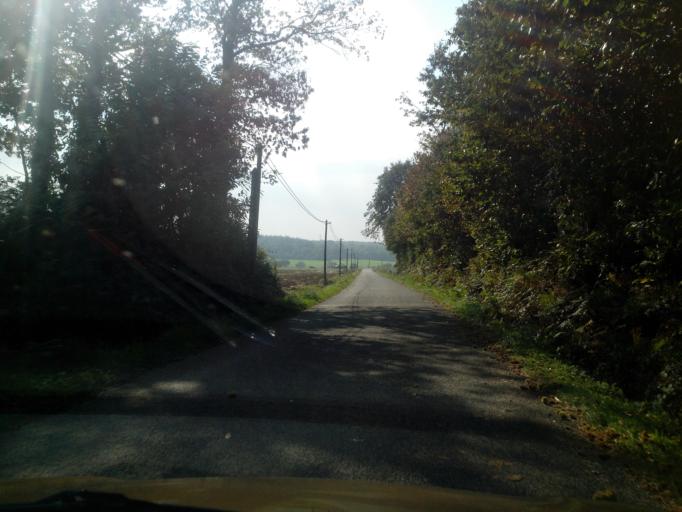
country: FR
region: Brittany
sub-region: Departement du Morbihan
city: Guilliers
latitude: 48.1051
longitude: -2.4001
